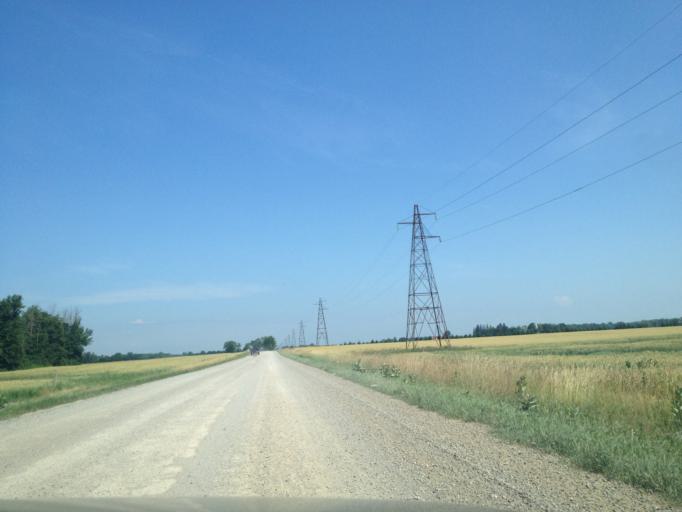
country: CA
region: Ontario
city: London
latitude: 43.1127
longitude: -81.2308
